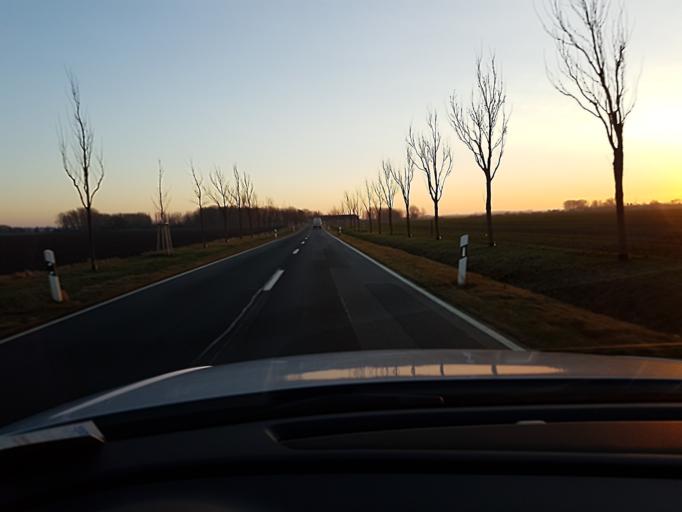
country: DE
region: Mecklenburg-Vorpommern
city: Wiek
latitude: 54.5930
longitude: 13.2893
